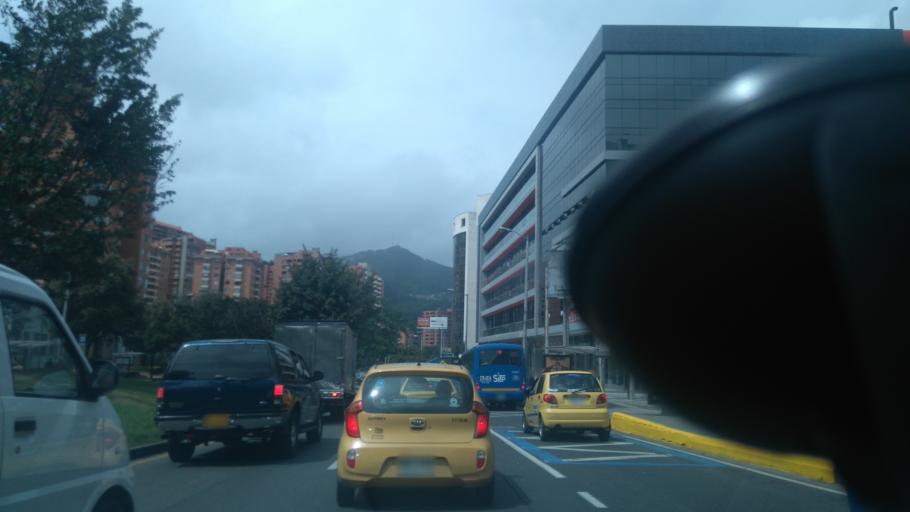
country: CO
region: Bogota D.C.
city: Barrio San Luis
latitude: 4.7039
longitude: -74.0288
